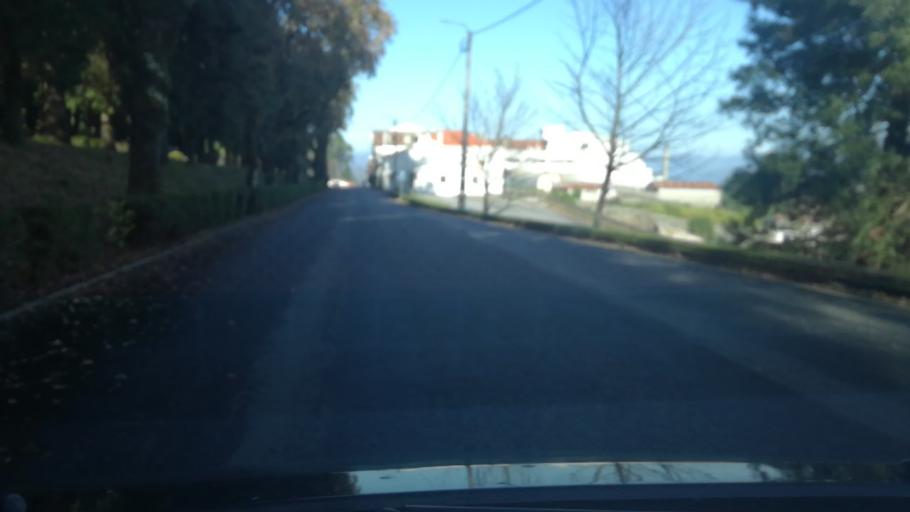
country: PT
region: Braga
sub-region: Braga
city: Braga
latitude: 41.5422
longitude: -8.3687
